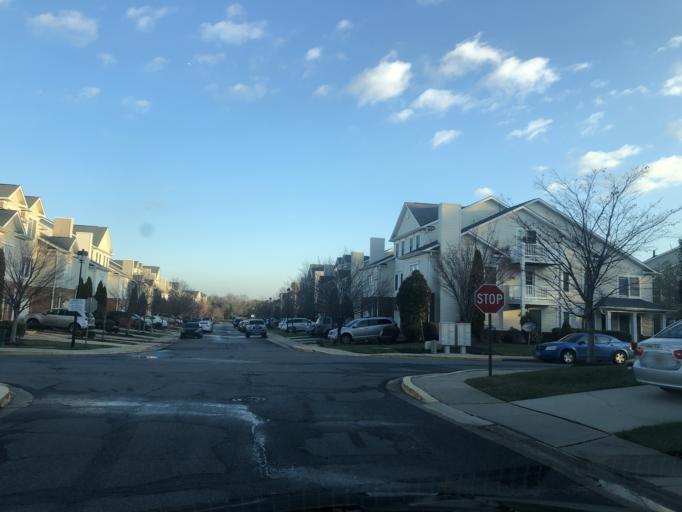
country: US
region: Maryland
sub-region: Anne Arundel County
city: Odenton
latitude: 39.0997
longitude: -76.7107
